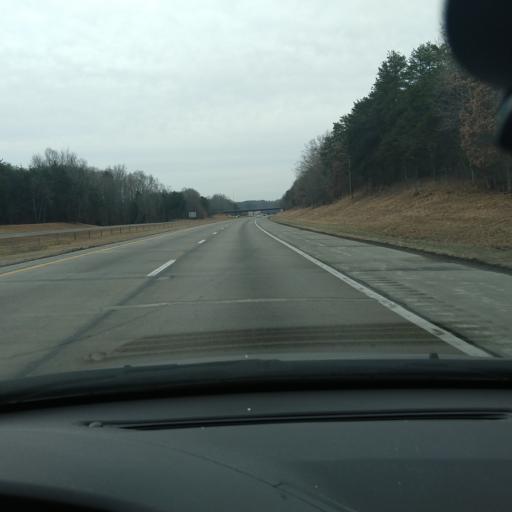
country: US
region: North Carolina
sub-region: Davidson County
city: Midway
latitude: 35.9624
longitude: -80.2307
